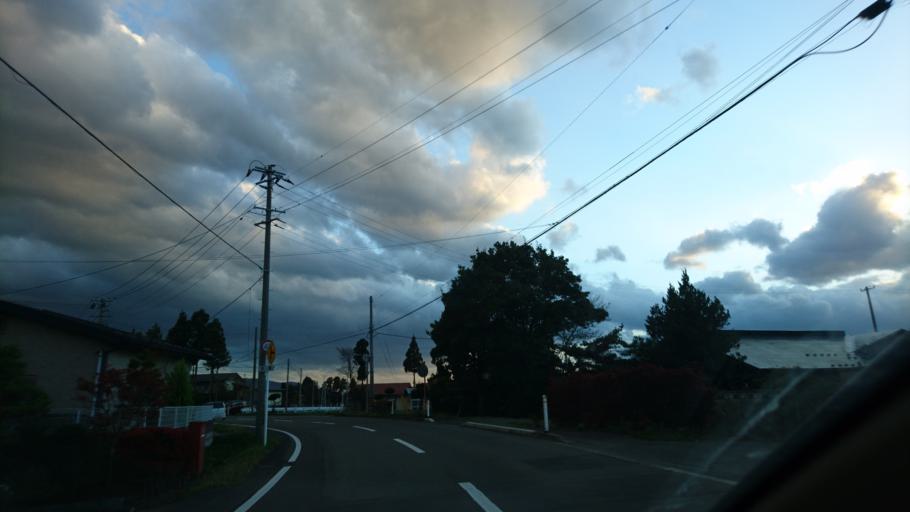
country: JP
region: Iwate
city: Mizusawa
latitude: 39.1121
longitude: 141.1503
